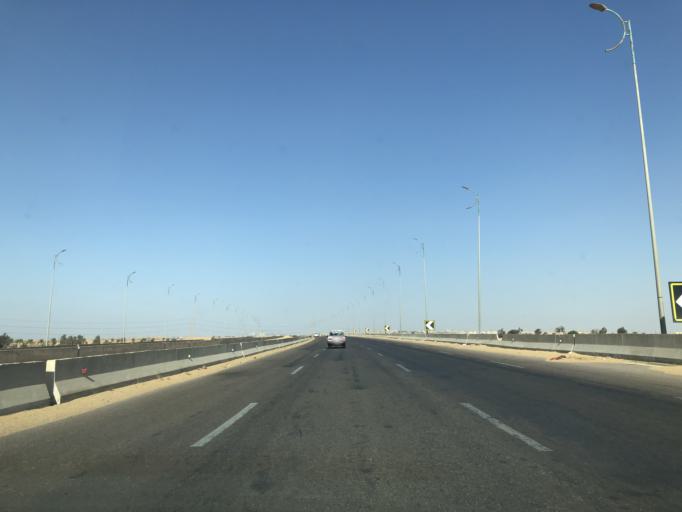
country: EG
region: Al Jizah
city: Awsim
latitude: 30.0683
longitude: 30.9033
